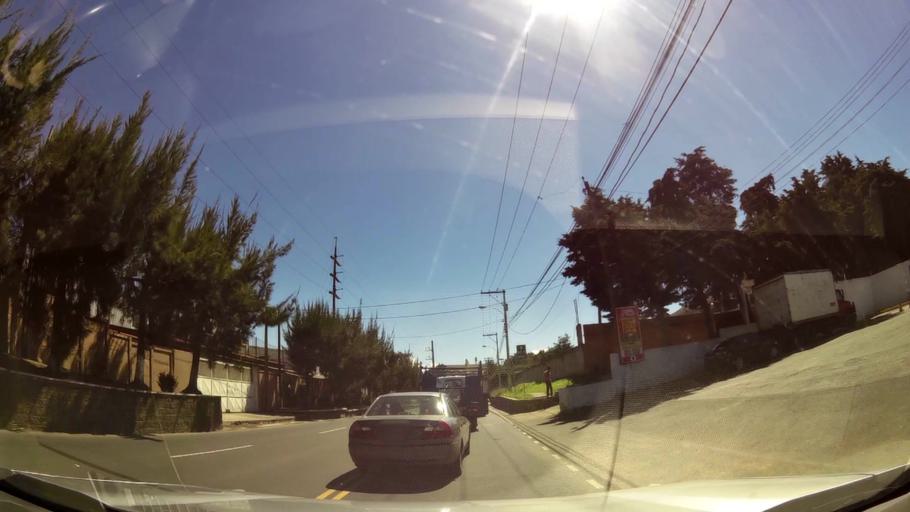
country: GT
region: Guatemala
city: San Jose Pinula
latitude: 14.5371
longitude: -90.4512
